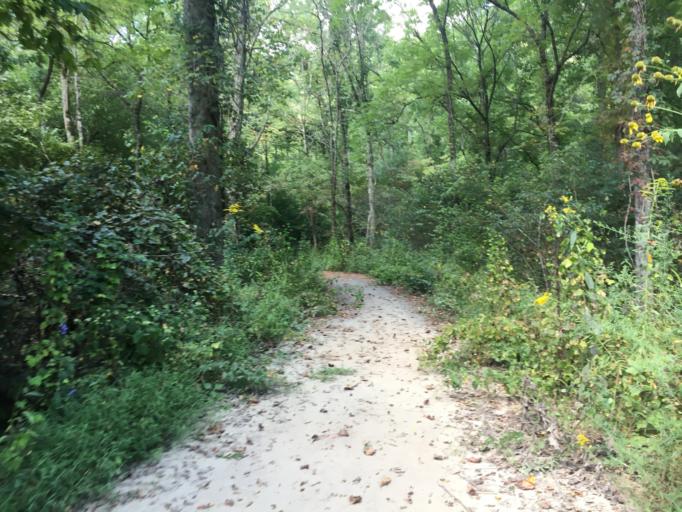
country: US
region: North Carolina
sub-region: Graham County
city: Robbinsville
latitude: 35.2747
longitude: -83.6795
